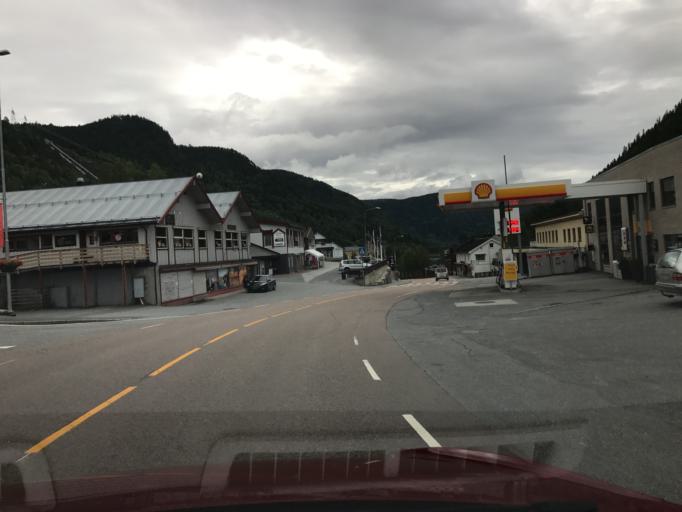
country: NO
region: Buskerud
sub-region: Nore og Uvdal
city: Rodberg
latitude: 60.2674
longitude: 8.9426
